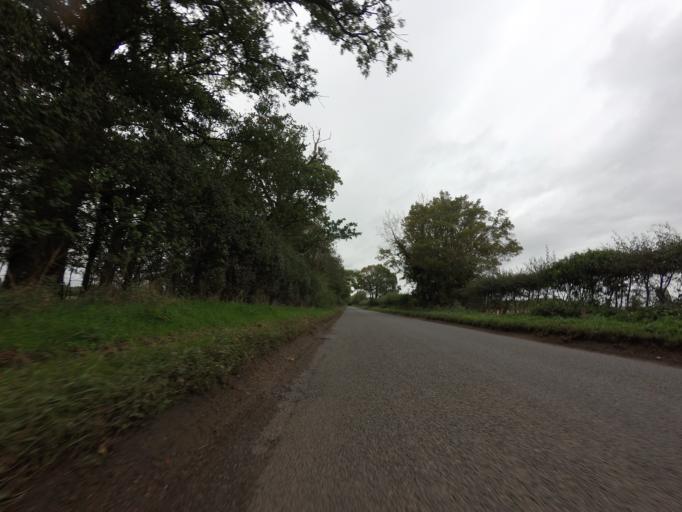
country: GB
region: England
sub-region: Cambridgeshire
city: Melbourn
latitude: 52.1055
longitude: 0.0489
